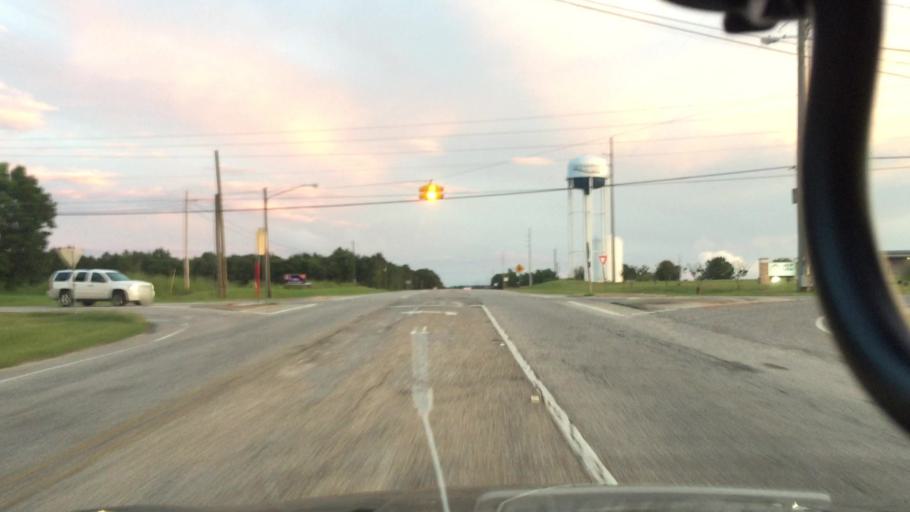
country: US
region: Alabama
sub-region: Coffee County
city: Enterprise
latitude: 31.3609
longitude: -85.8671
